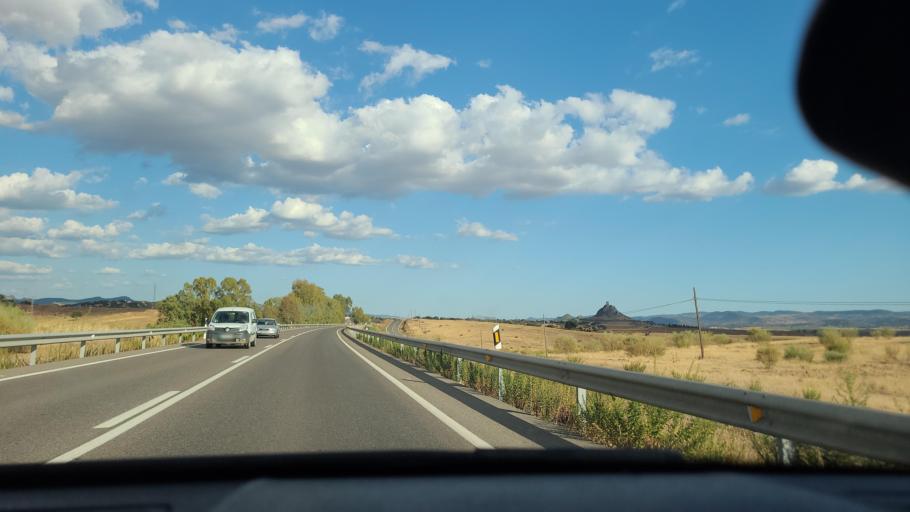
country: ES
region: Andalusia
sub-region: Province of Cordoba
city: Penarroya-Pueblonuevo
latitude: 38.2949
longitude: -5.2359
